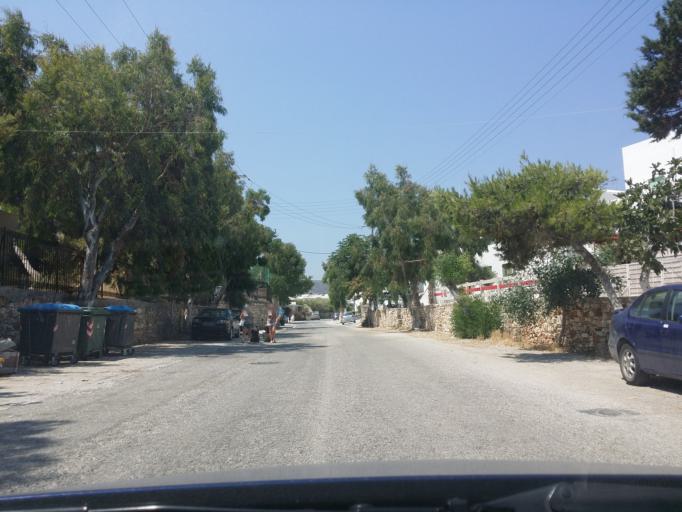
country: GR
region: South Aegean
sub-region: Nomos Kykladon
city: Naousa
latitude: 37.1194
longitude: 25.2368
